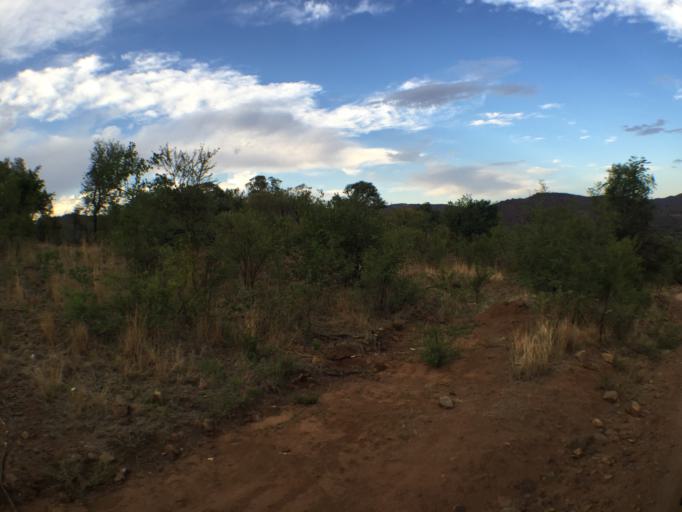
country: ZA
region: North-West
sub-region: Bojanala Platinum District Municipality
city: Mogwase
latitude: -25.2234
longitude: 27.0677
